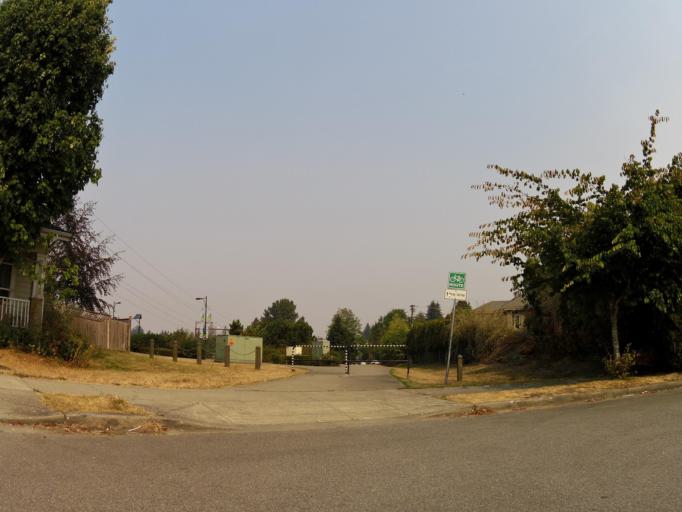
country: CA
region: British Columbia
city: Delta
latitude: 49.1550
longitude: -122.9234
